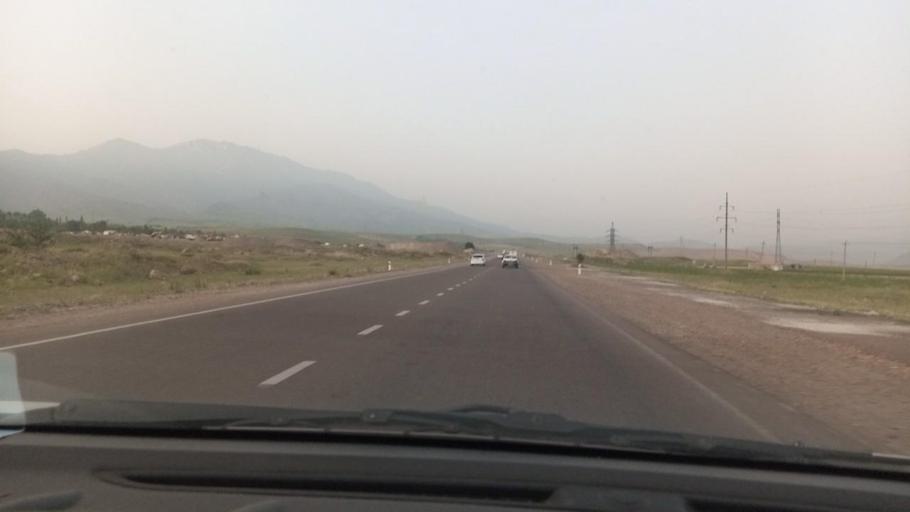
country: UZ
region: Toshkent
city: Angren
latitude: 41.0413
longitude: 70.1521
